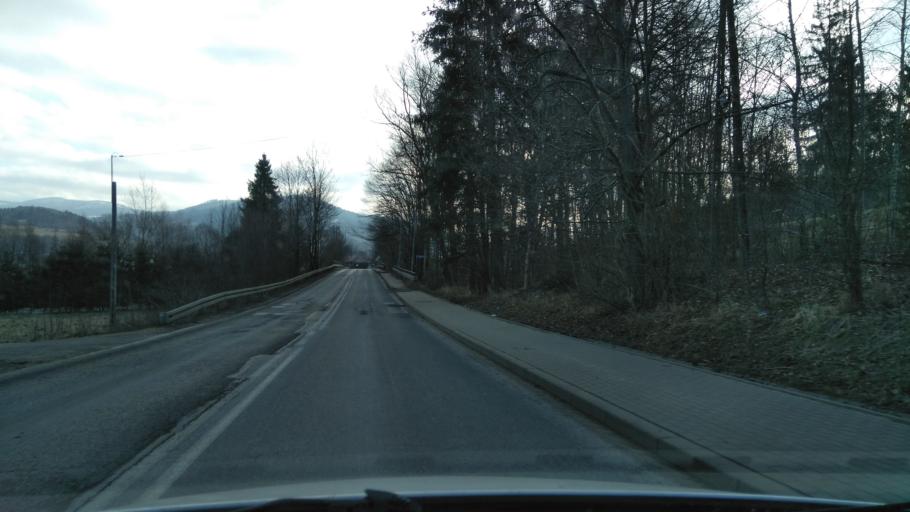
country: PL
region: Silesian Voivodeship
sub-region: Powiat zywiecki
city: Milowka
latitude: 49.5616
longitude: 19.0809
